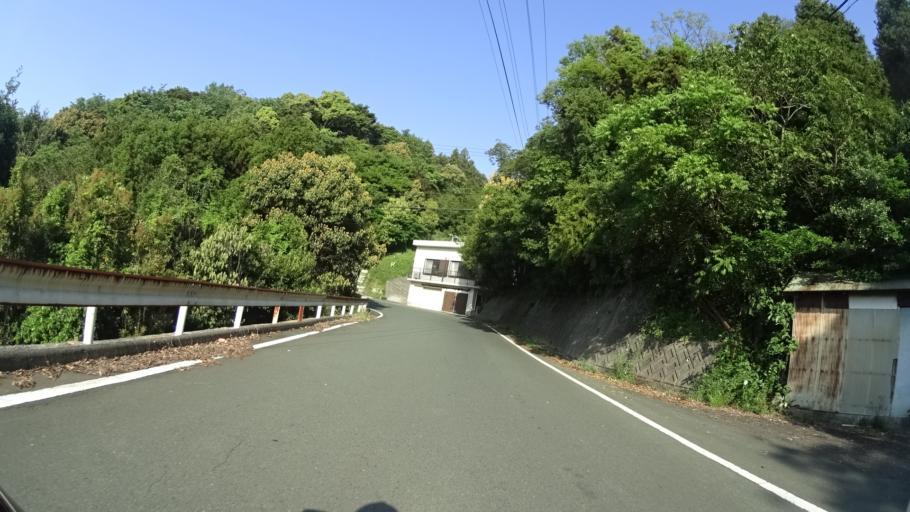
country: JP
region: Ehime
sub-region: Nishiuwa-gun
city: Ikata-cho
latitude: 33.3837
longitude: 132.0852
